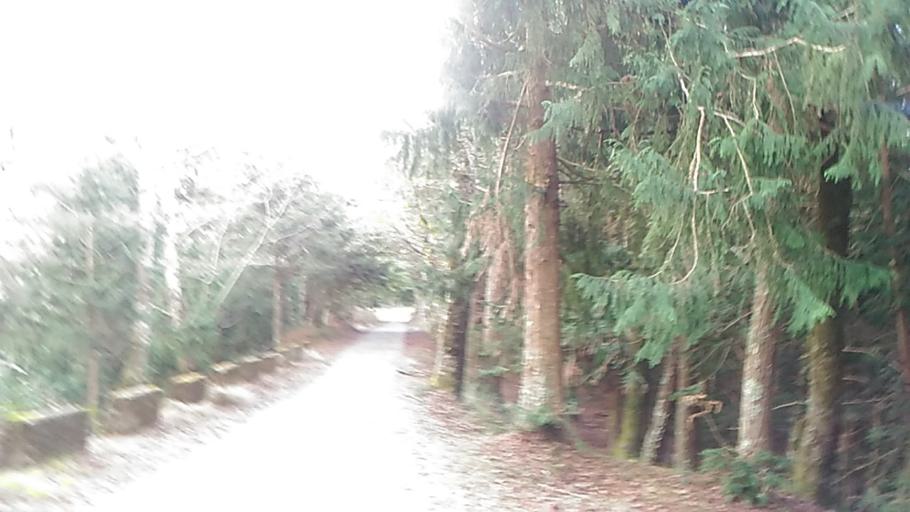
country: TW
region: Taiwan
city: Daxi
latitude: 24.4080
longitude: 121.3046
